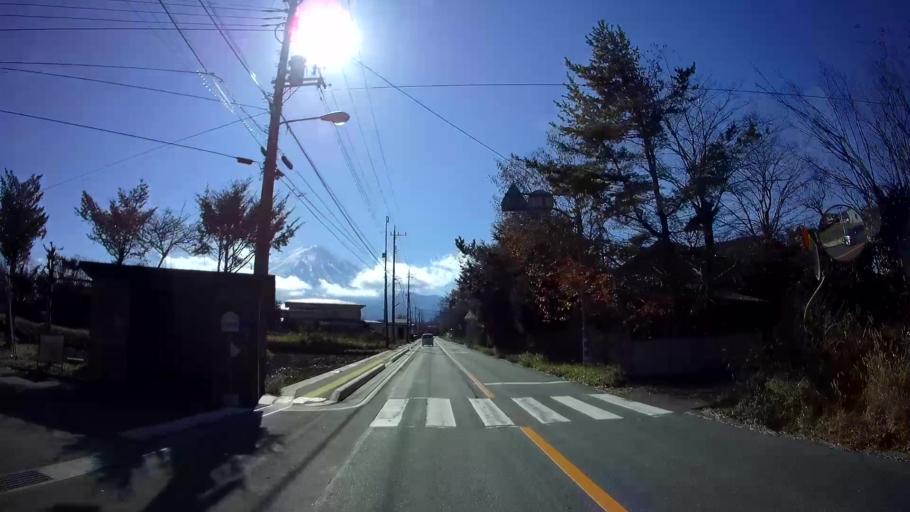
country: JP
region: Yamanashi
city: Fujikawaguchiko
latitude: 35.4895
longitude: 138.7277
